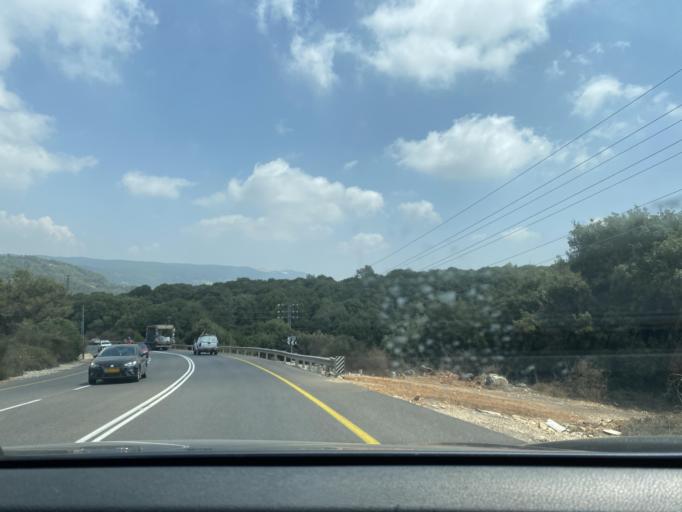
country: IL
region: Northern District
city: Kefar Weradim
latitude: 33.0027
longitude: 35.2868
